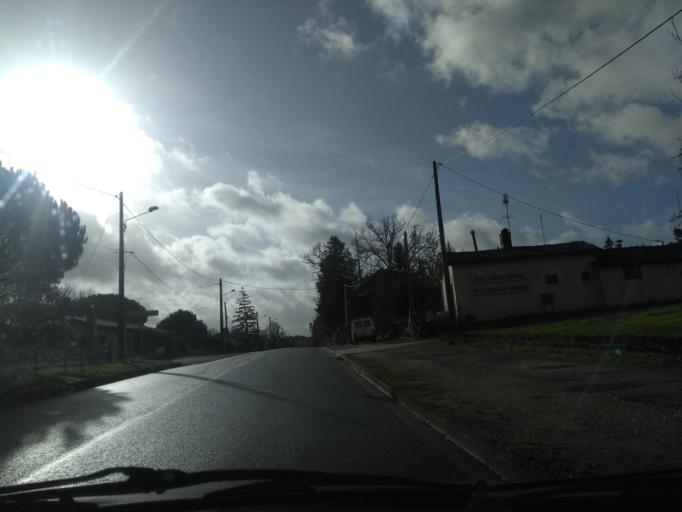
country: FR
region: Aquitaine
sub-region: Departement de la Gironde
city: Belin-Beliet
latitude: 44.4909
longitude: -0.7910
